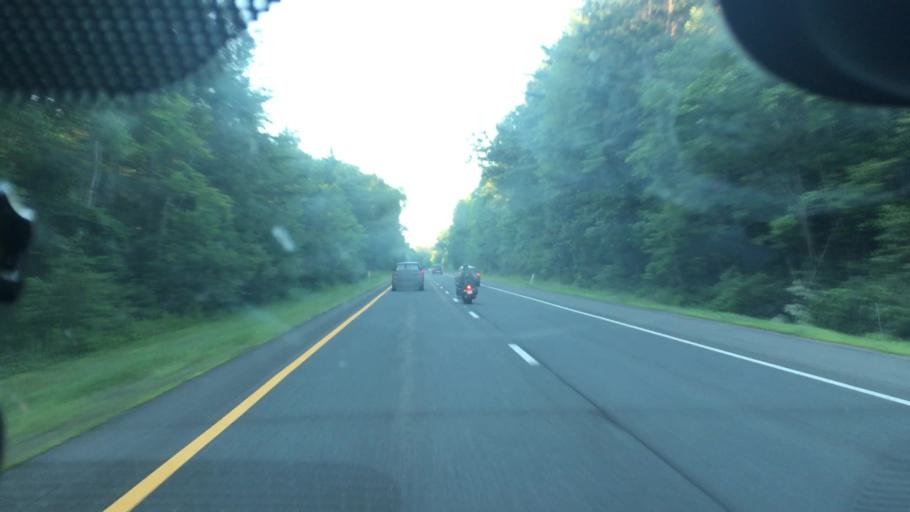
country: US
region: Massachusetts
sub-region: Franklin County
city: Turners Falls
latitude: 42.6253
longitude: -72.5851
